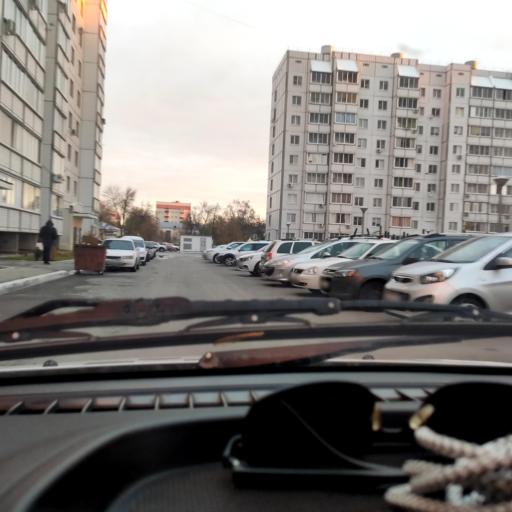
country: RU
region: Samara
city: Tol'yatti
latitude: 53.5194
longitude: 49.4214
